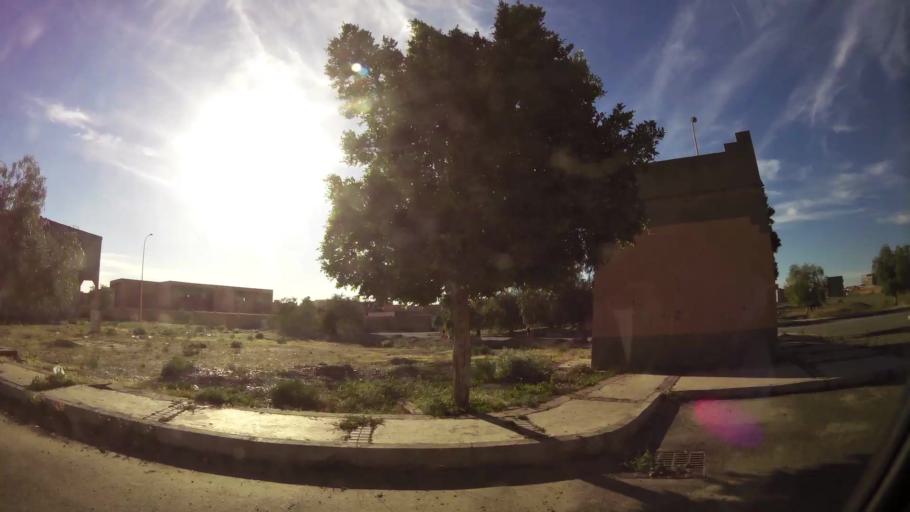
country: MA
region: Marrakech-Tensift-Al Haouz
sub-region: Marrakech
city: Marrakesh
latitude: 31.7613
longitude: -8.0961
